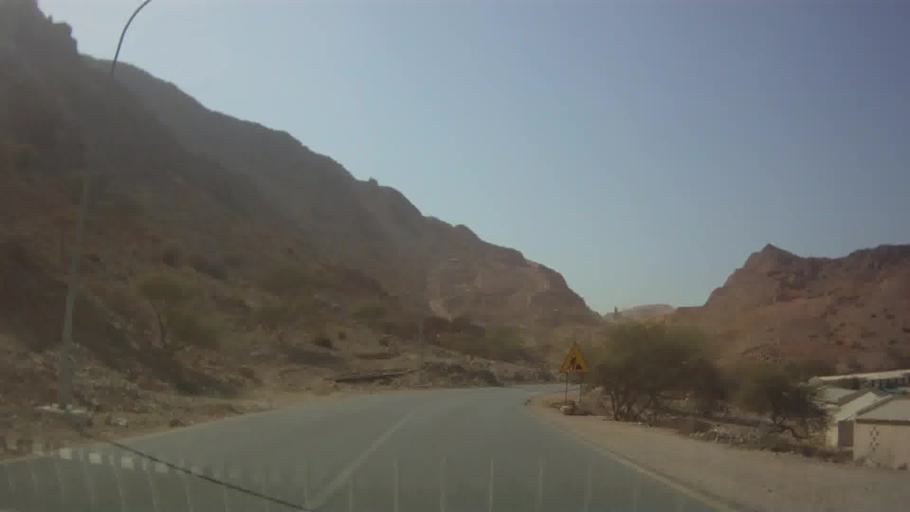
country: OM
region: Muhafazat Masqat
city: Muscat
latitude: 23.5066
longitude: 58.7291
